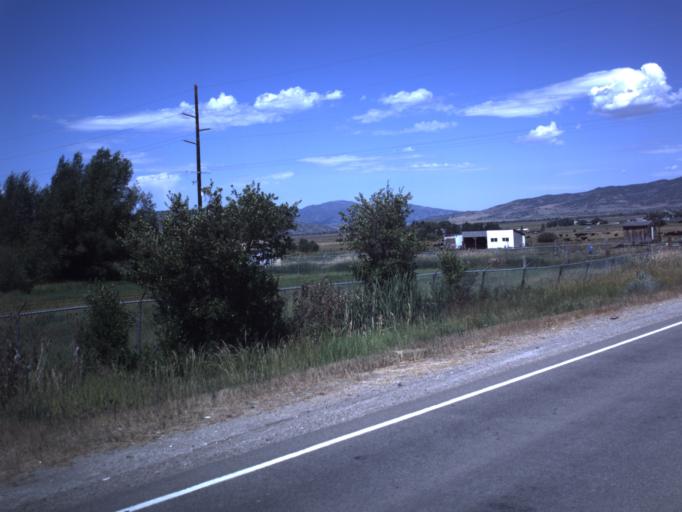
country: US
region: Utah
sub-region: Summit County
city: Kamas
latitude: 40.6540
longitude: -111.2808
